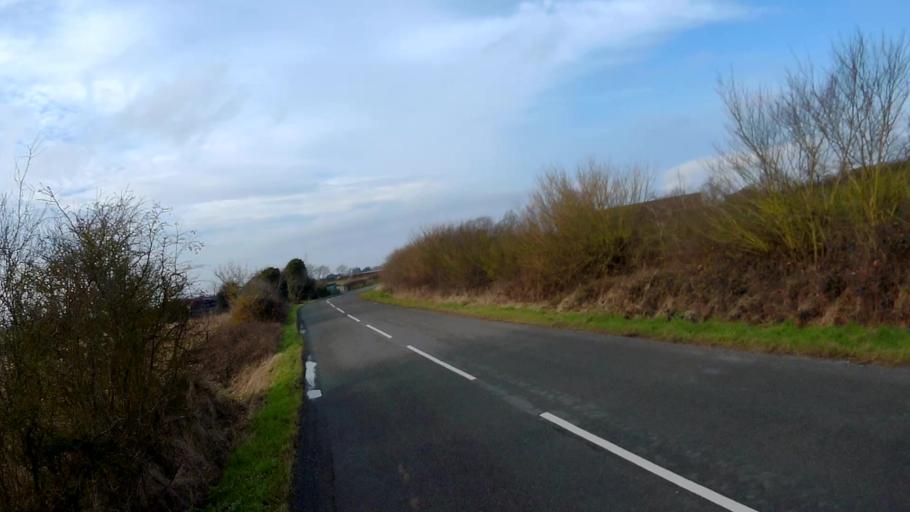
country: GB
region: England
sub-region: Lincolnshire
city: Bourne
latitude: 52.7372
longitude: -0.3977
